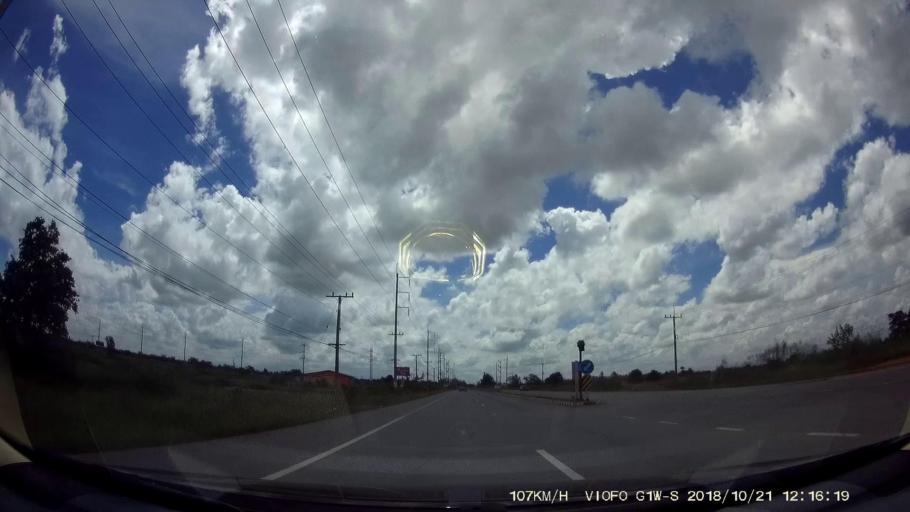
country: TH
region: Nakhon Ratchasima
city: Dan Khun Thot
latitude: 15.3493
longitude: 101.8264
